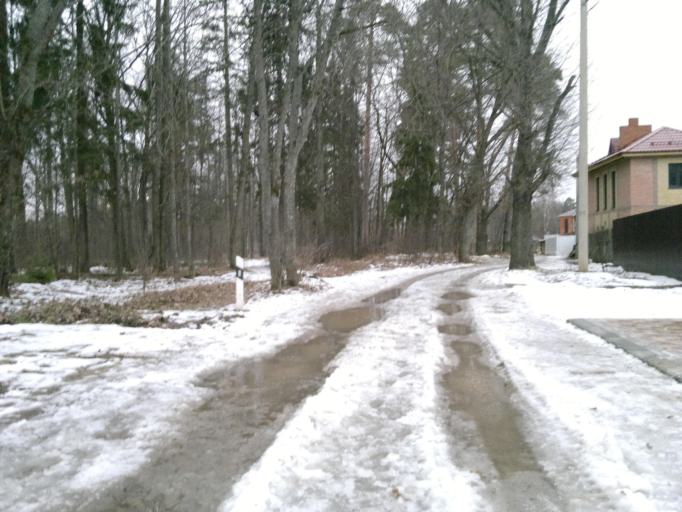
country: RU
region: Mariy-El
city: Yoshkar-Ola
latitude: 56.6152
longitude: 47.9448
